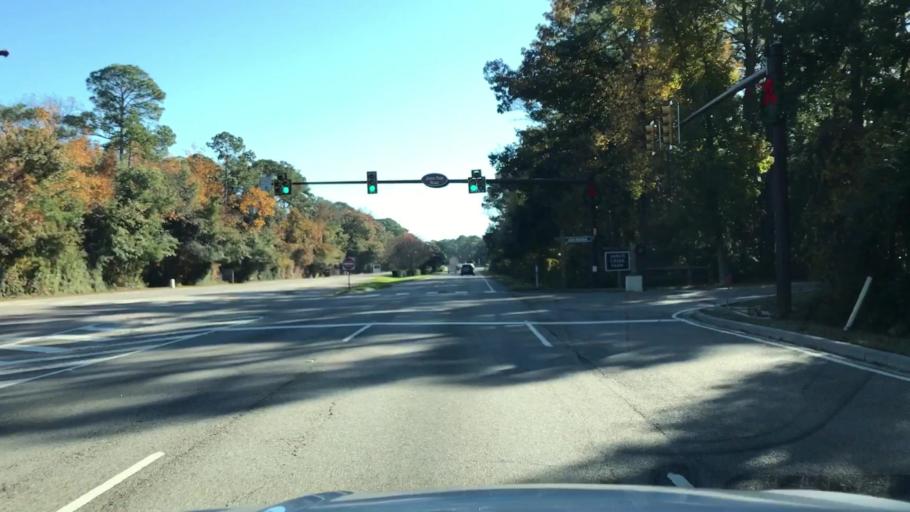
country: US
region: South Carolina
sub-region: Beaufort County
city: Hilton Head Island
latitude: 32.2146
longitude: -80.7334
